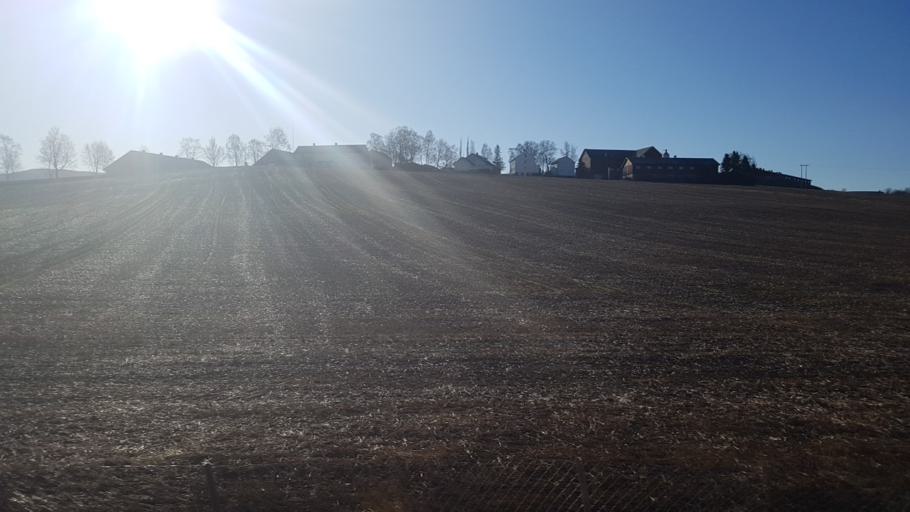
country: NO
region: Nord-Trondelag
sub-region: Levanger
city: Skogn
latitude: 63.6925
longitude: 11.1773
